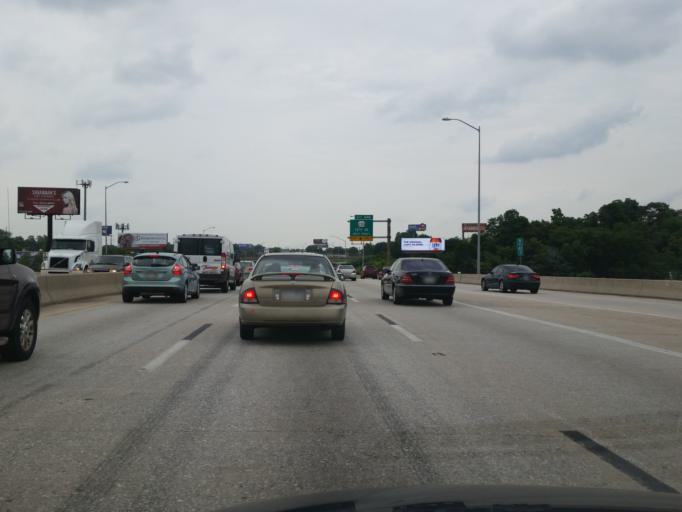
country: US
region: Pennsylvania
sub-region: Cumberland County
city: New Cumberland
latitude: 40.2524
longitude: -76.8697
